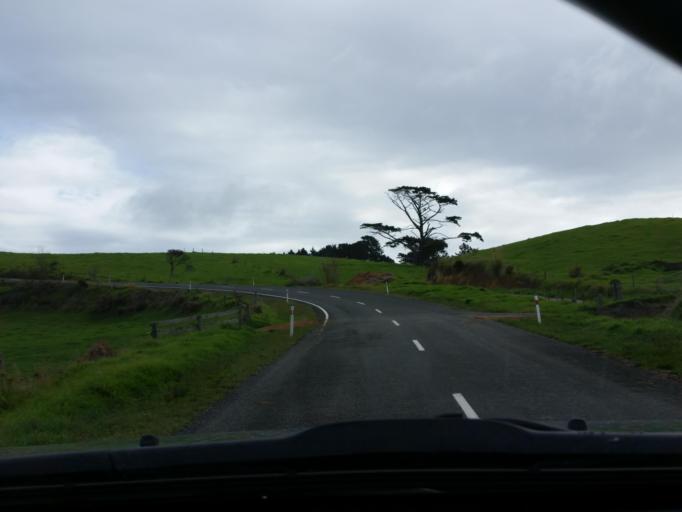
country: NZ
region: Northland
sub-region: Kaipara District
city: Dargaville
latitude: -36.0284
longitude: 173.8656
